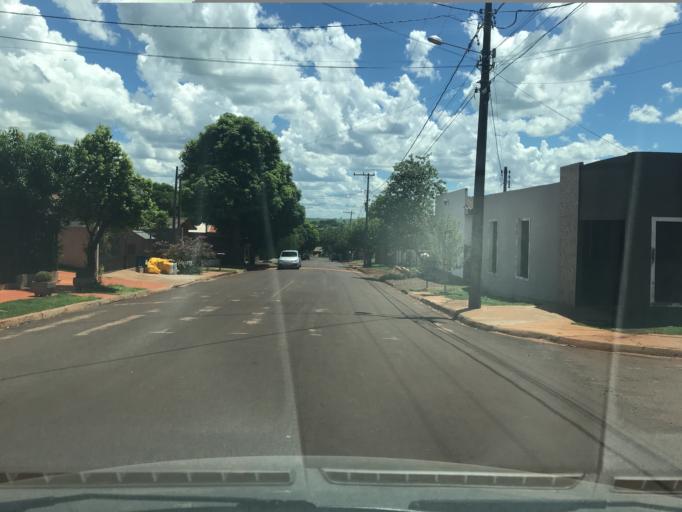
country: BR
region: Parana
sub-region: Palotina
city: Palotina
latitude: -24.2778
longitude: -53.8467
